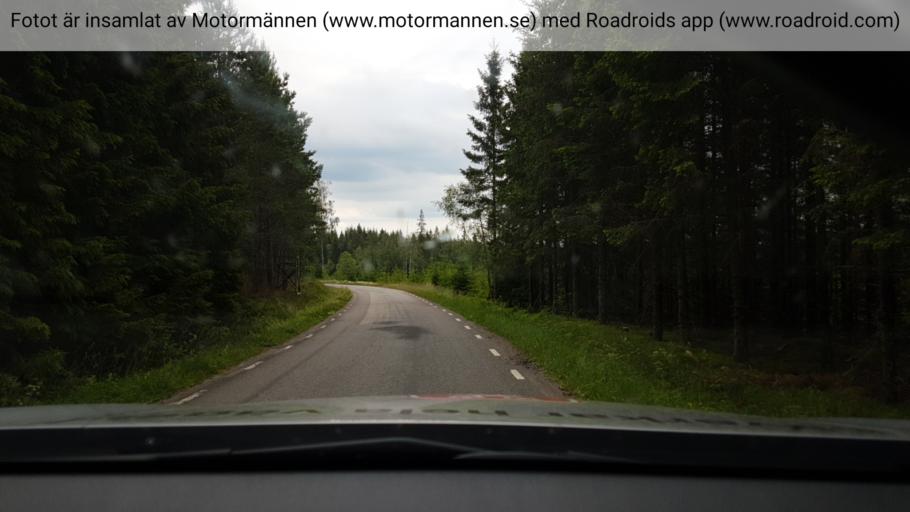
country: SE
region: Joenkoeping
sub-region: Mullsjo Kommun
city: Mullsjoe
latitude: 57.9543
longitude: 13.7094
